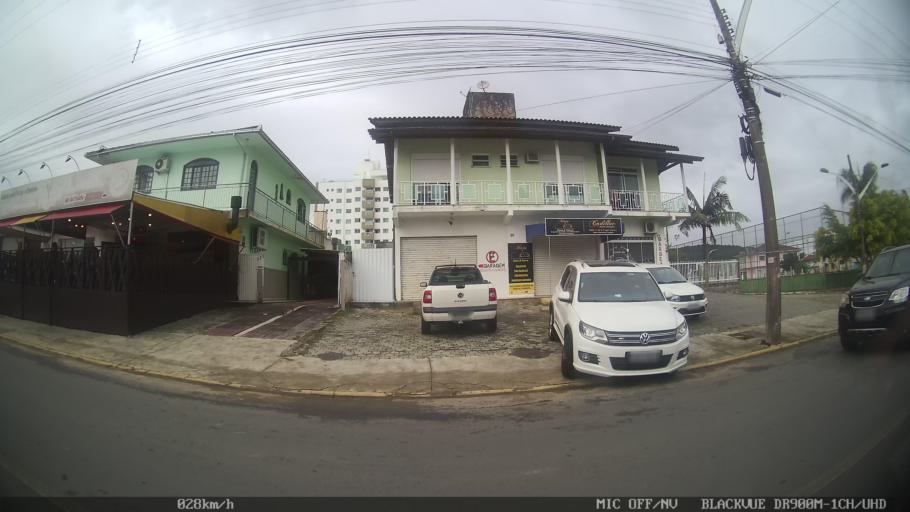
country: BR
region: Santa Catarina
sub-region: Biguacu
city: Biguacu
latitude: -27.5086
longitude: -48.6520
